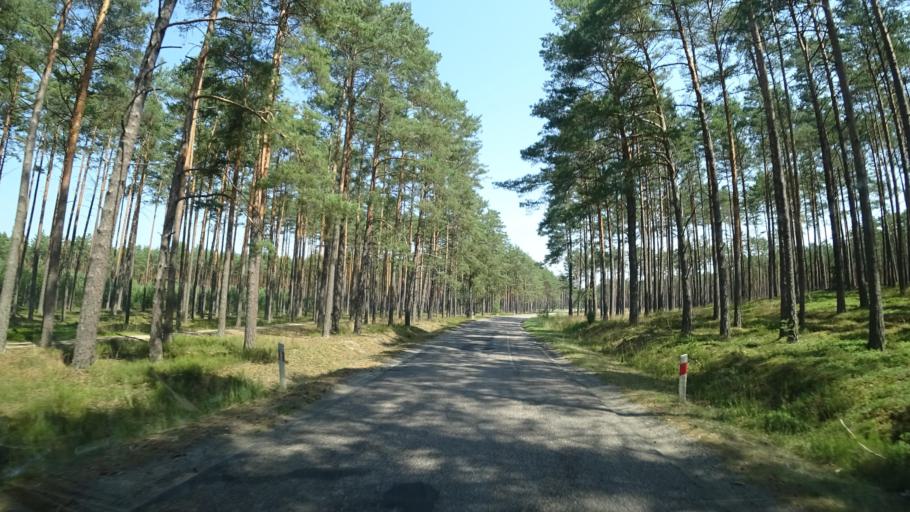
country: PL
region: Pomeranian Voivodeship
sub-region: Powiat chojnicki
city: Brusy
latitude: 53.8611
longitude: 17.6016
